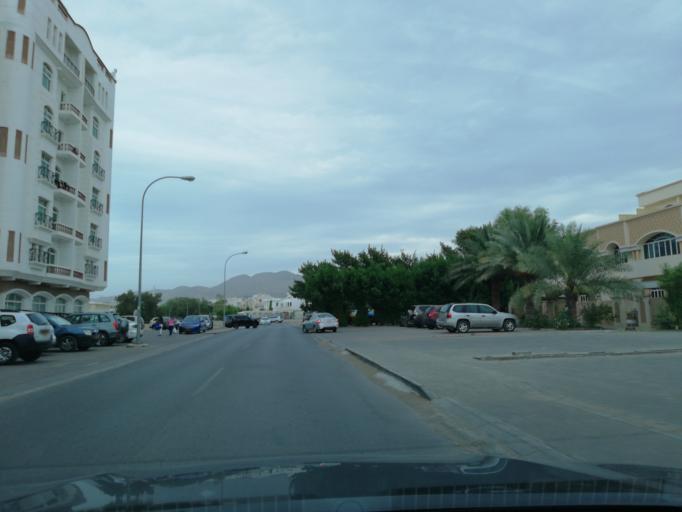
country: OM
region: Muhafazat Masqat
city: Bawshar
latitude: 23.5804
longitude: 58.3942
